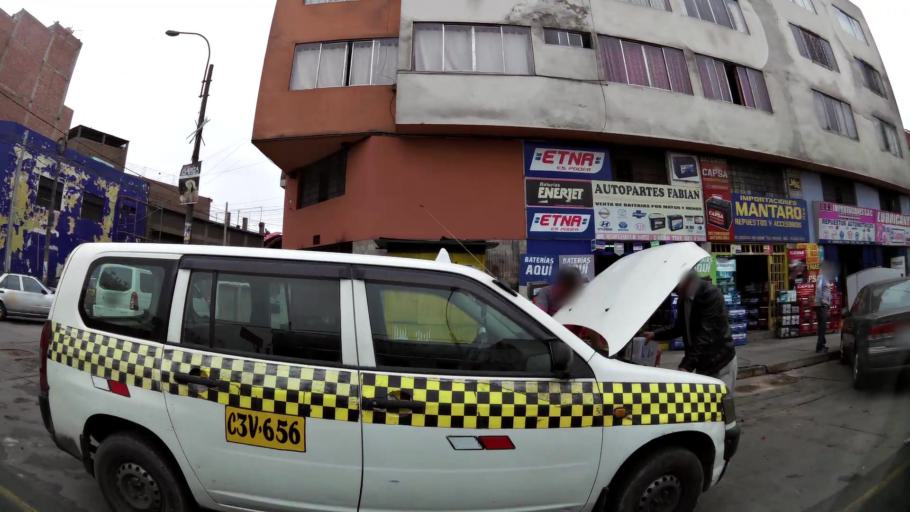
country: PE
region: Lima
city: Lima
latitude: -12.0555
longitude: -77.0539
